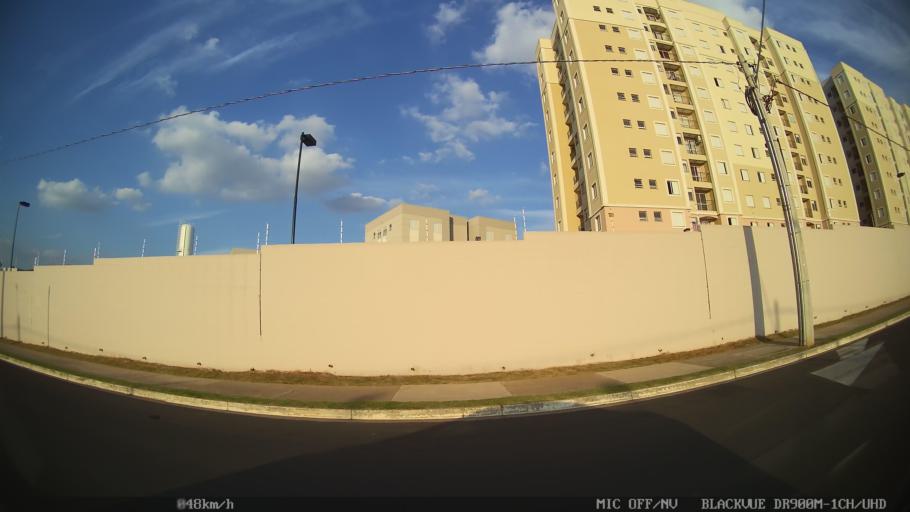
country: BR
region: Sao Paulo
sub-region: Hortolandia
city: Hortolandia
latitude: -22.8942
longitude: -47.1622
